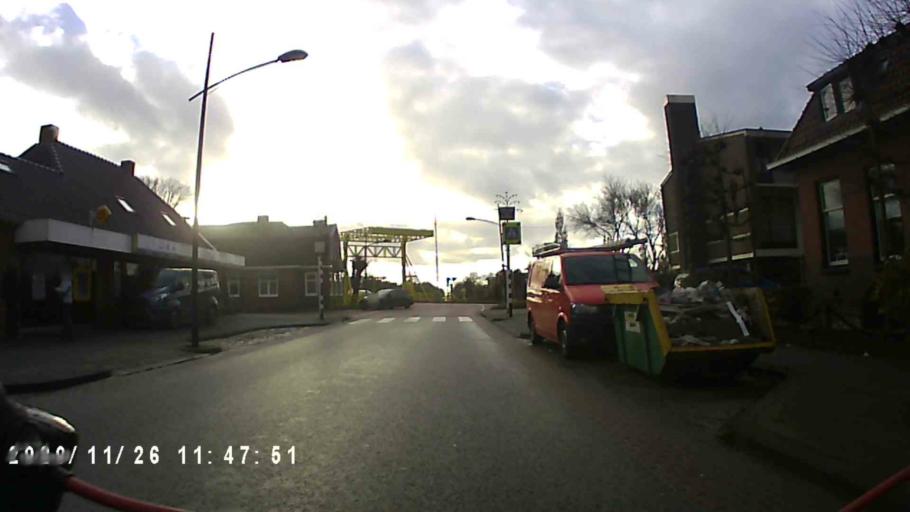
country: NL
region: Groningen
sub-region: Gemeente Bedum
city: Bedum
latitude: 53.3011
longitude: 6.5963
